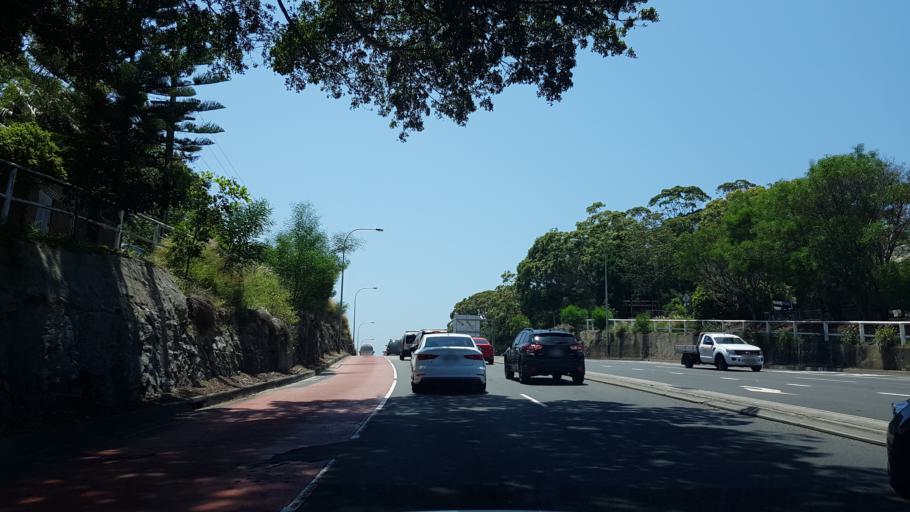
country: AU
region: New South Wales
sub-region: Warringah
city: Narraweena
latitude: -33.7583
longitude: 151.2807
